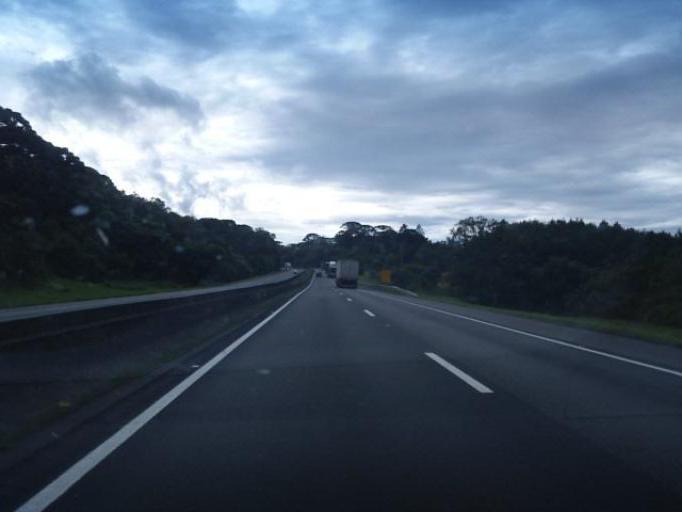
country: BR
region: Parana
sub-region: Campina Grande Do Sul
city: Campina Grande do Sul
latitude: -25.3066
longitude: -48.9909
